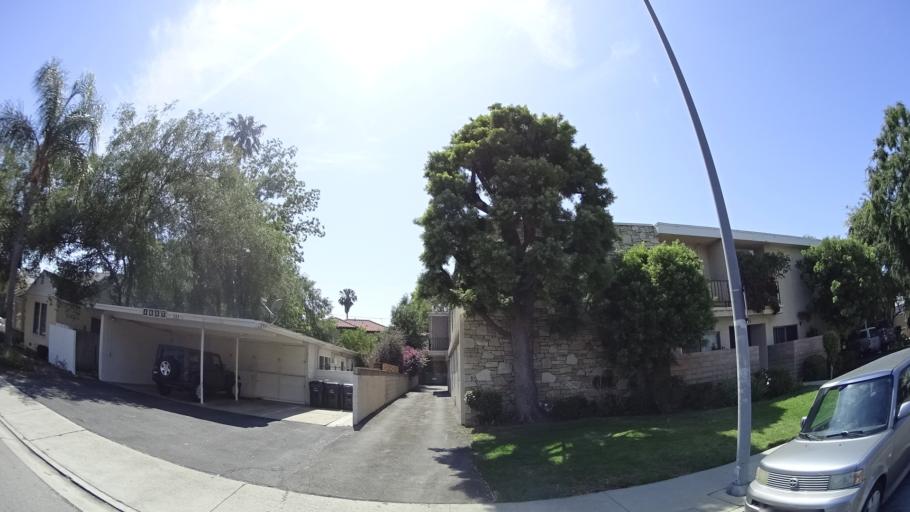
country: US
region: California
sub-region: Los Angeles County
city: Sherman Oaks
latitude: 34.1616
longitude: -118.4575
